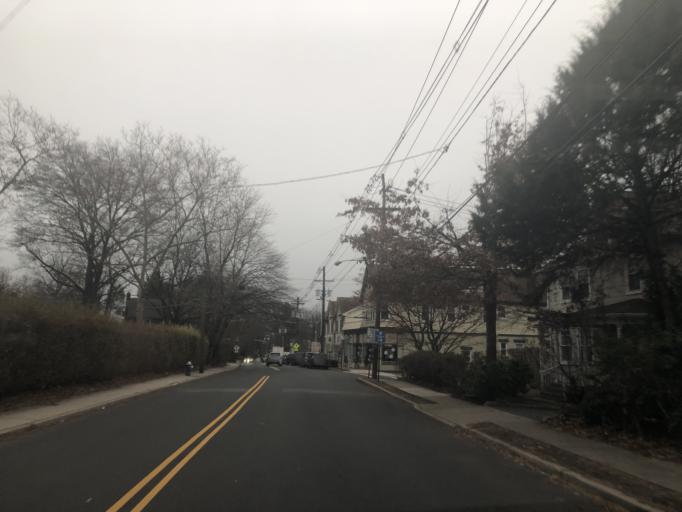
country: US
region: New Jersey
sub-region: Essex County
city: Maplewood
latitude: 40.7346
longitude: -74.2688
